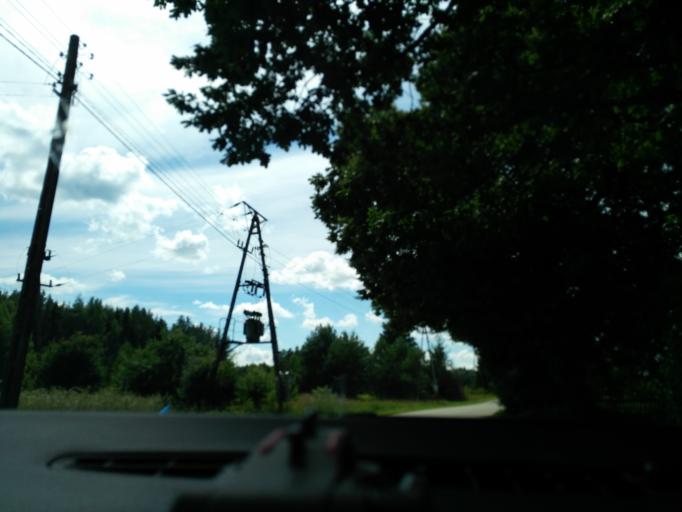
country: PL
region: Podlasie
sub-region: Powiat sejnenski
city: Sejny
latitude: 54.0324
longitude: 23.3482
